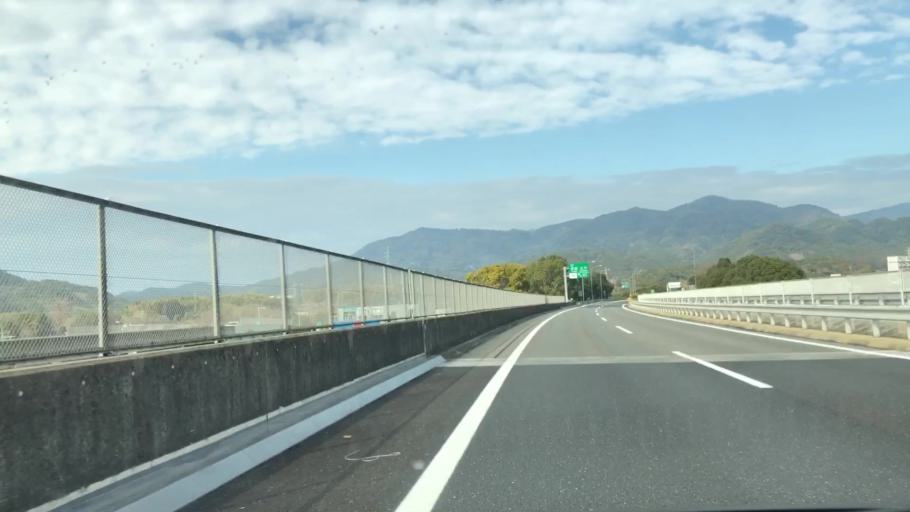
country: JP
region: Saga Prefecture
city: Takeocho-takeo
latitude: 33.2145
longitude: 130.0514
